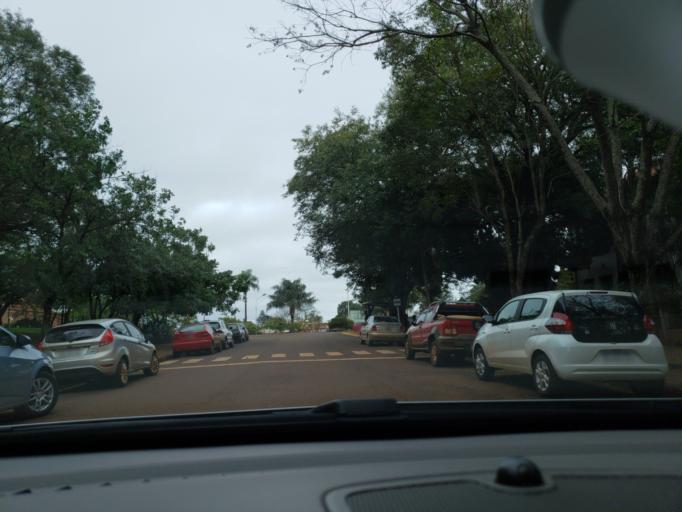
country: AR
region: Misiones
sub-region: Departamento de Apostoles
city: Apostoles
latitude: -27.9139
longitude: -55.7555
